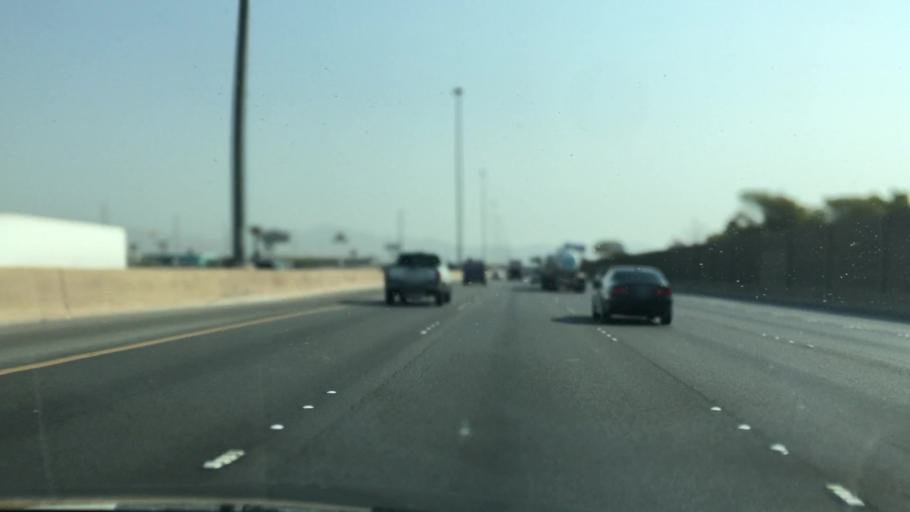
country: US
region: Nevada
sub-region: Clark County
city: North Las Vegas
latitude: 36.2090
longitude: -115.1299
